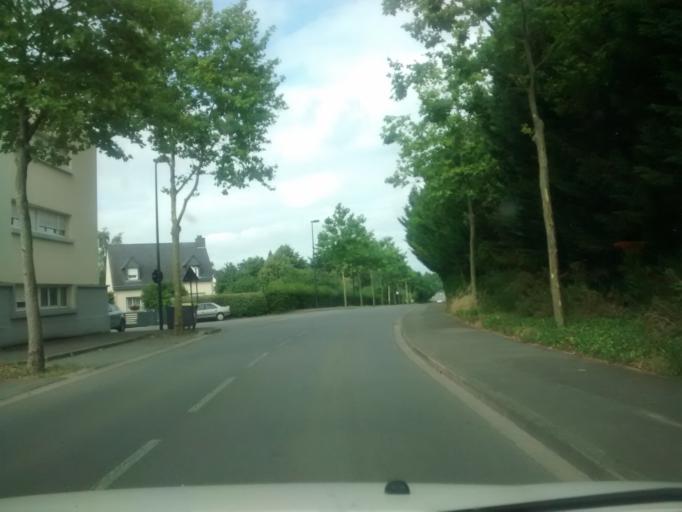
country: FR
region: Brittany
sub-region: Departement d'Ille-et-Vilaine
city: Saint-Jacques-de-la-Lande
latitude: 48.0867
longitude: -1.7110
